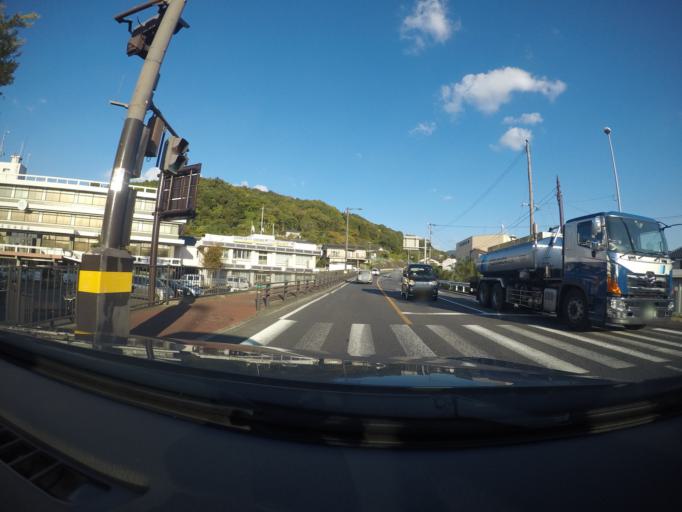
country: JP
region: Kumamoto
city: Minamata
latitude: 32.2113
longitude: 130.4085
